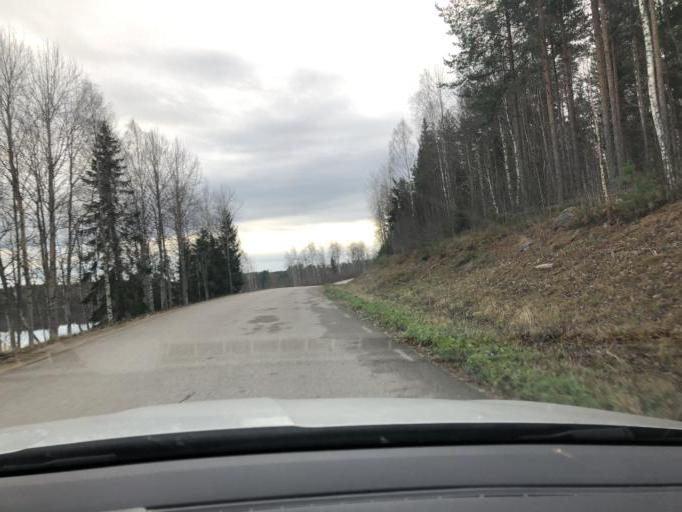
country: SE
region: Gaevleborg
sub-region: Hudiksvalls Kommun
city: Sorforsa
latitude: 61.6655
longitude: 16.9263
